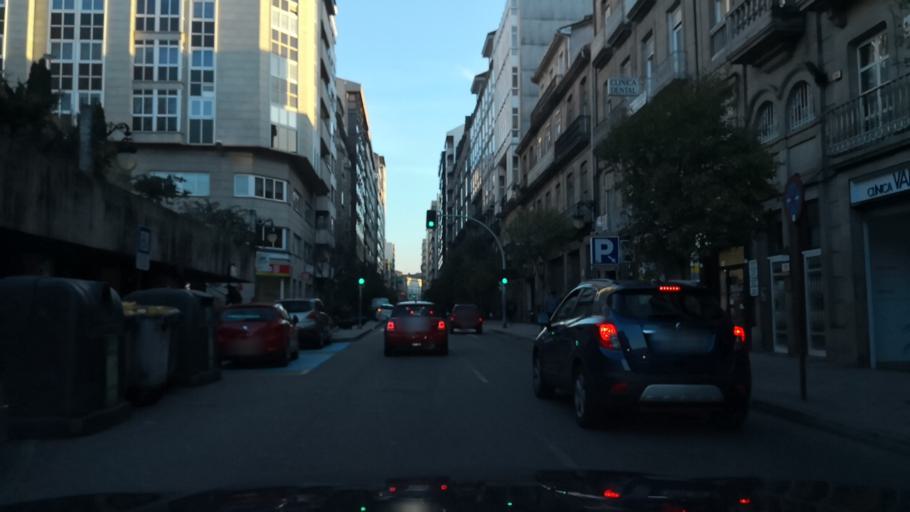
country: ES
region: Galicia
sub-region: Provincia de Ourense
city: Ourense
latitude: 42.3419
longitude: -7.8677
